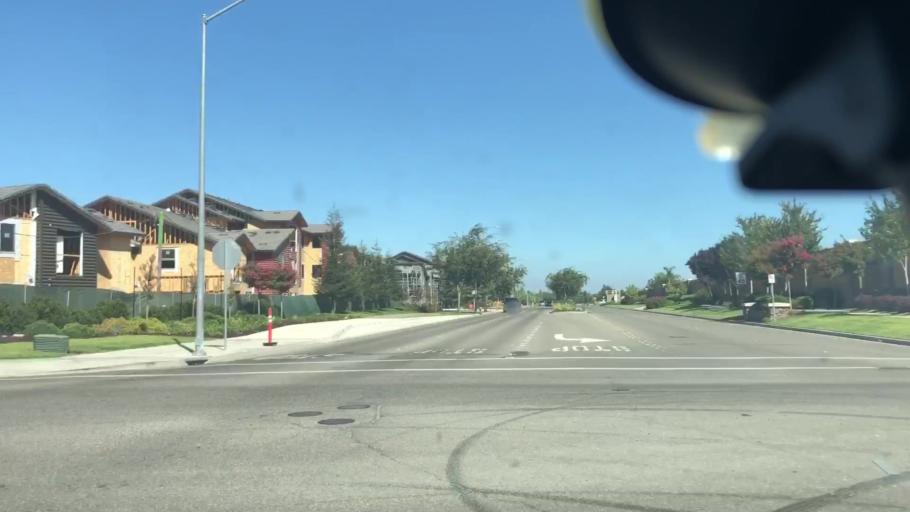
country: US
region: California
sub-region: San Joaquin County
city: Manteca
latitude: 37.7816
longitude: -121.2007
